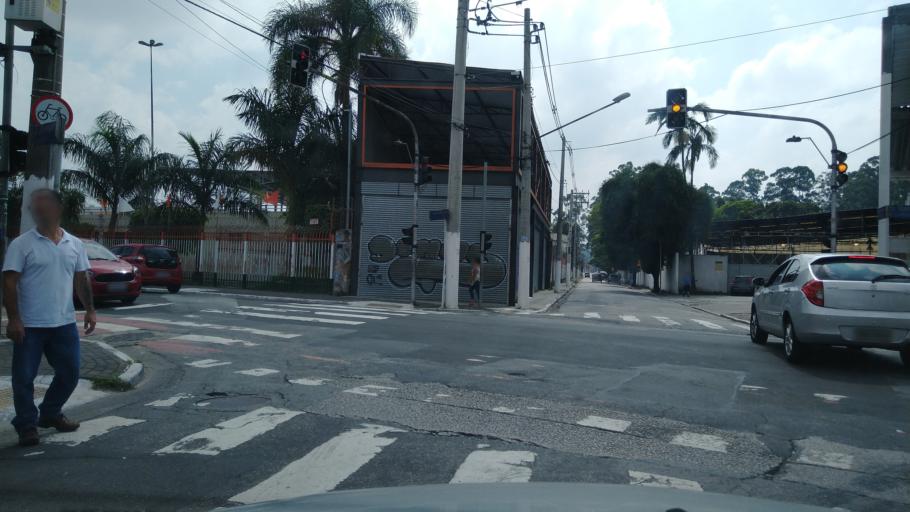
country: BR
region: Sao Paulo
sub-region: Guarulhos
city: Guarulhos
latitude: -23.4687
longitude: -46.5797
